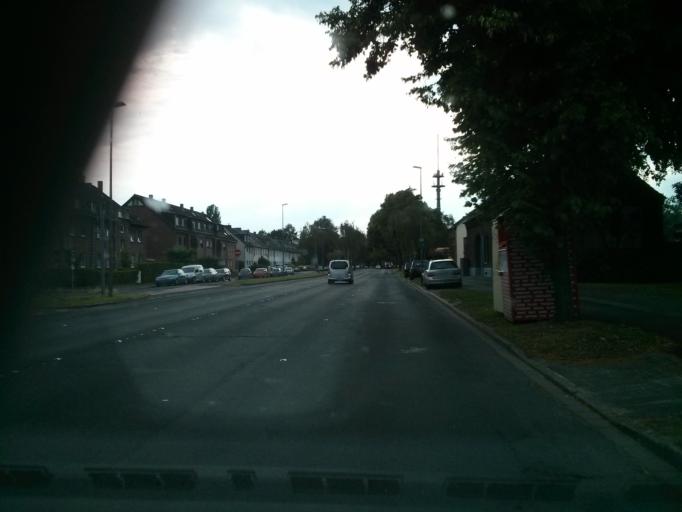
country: DE
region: North Rhine-Westphalia
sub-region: Regierungsbezirk Dusseldorf
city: Krefeld
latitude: 51.3369
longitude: 6.6069
